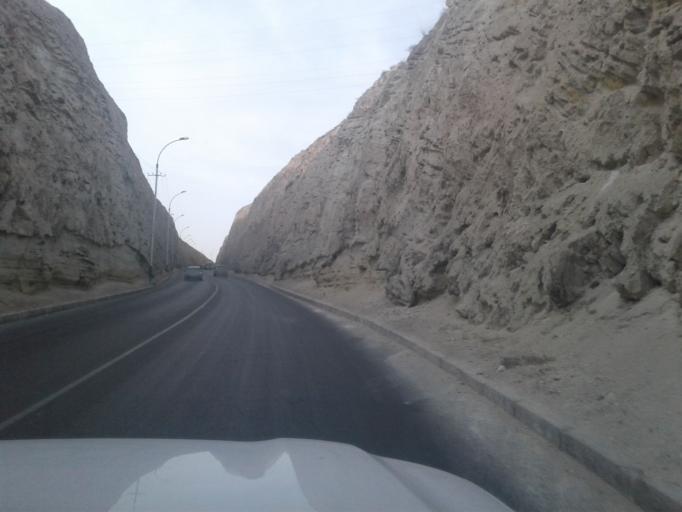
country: TM
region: Balkan
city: Turkmenbasy
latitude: 40.0370
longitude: 52.9699
